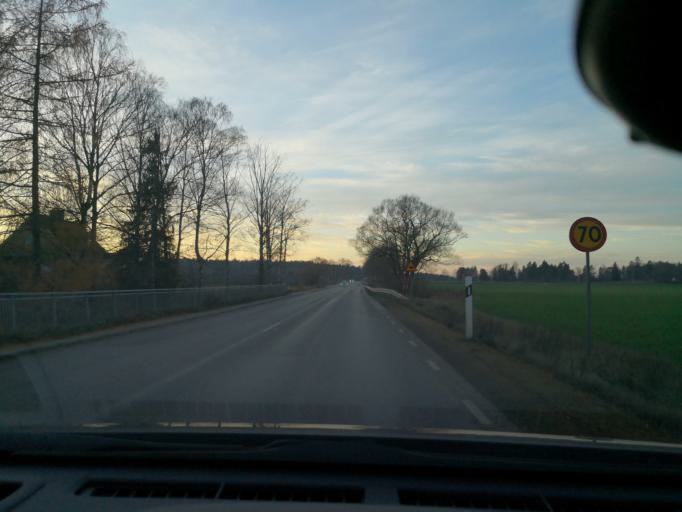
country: SE
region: Vaestmanland
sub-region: Kopings Kommun
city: Koping
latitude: 59.5128
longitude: 16.0329
